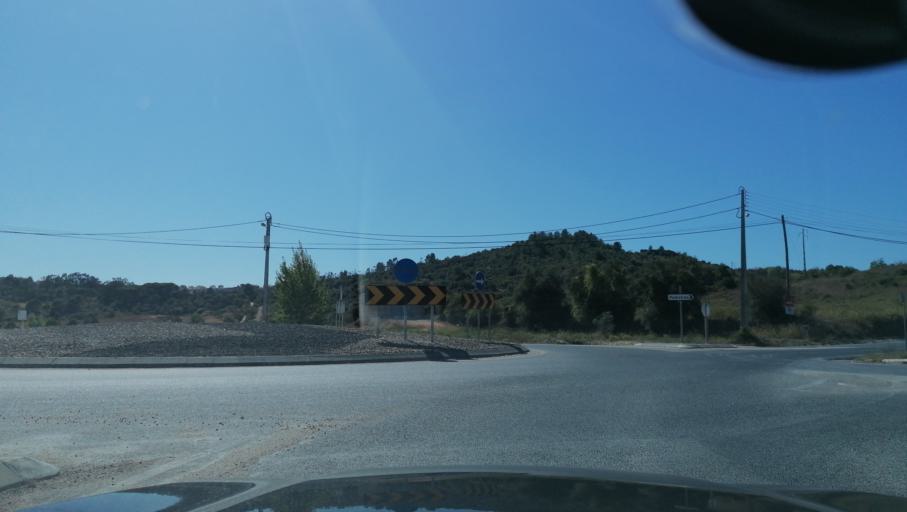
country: PT
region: Lisbon
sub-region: Alenquer
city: Alenquer
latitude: 39.0669
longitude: -9.0051
